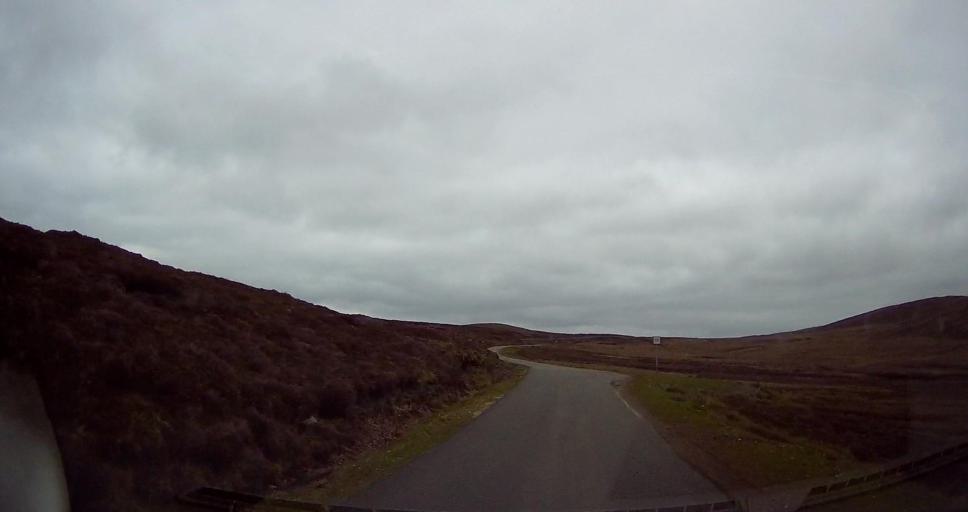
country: GB
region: Scotland
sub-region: Shetland Islands
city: Lerwick
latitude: 60.3142
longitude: -1.3420
